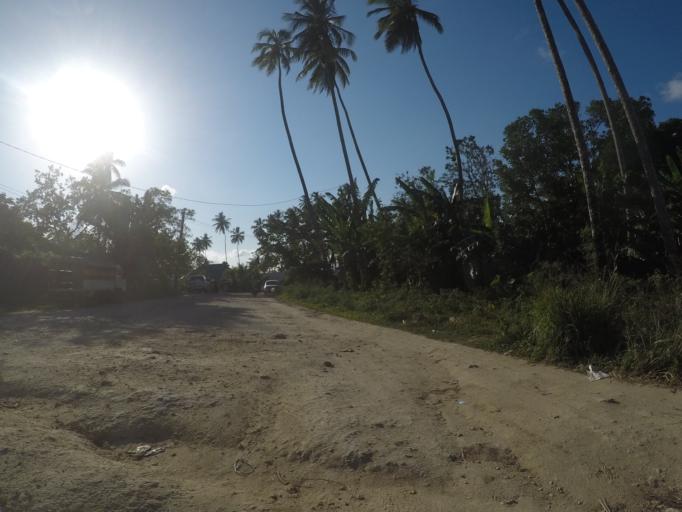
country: TZ
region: Zanzibar Central/South
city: Koani
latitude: -6.1408
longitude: 39.2841
